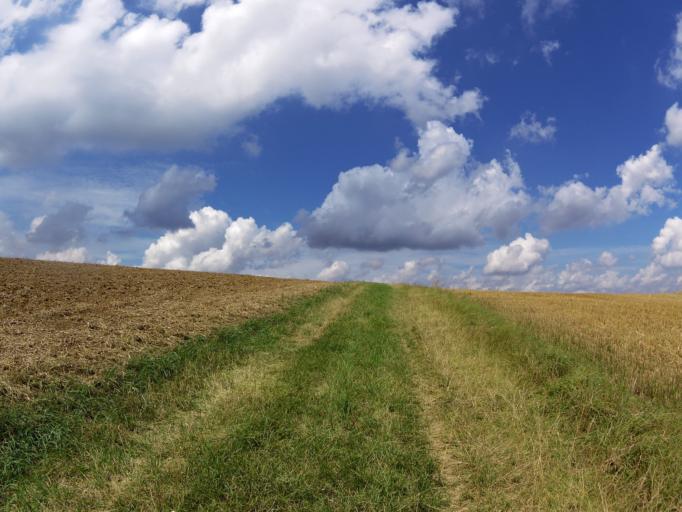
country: DE
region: Bavaria
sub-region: Regierungsbezirk Unterfranken
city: Reichenberg
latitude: 49.7123
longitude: 9.9105
